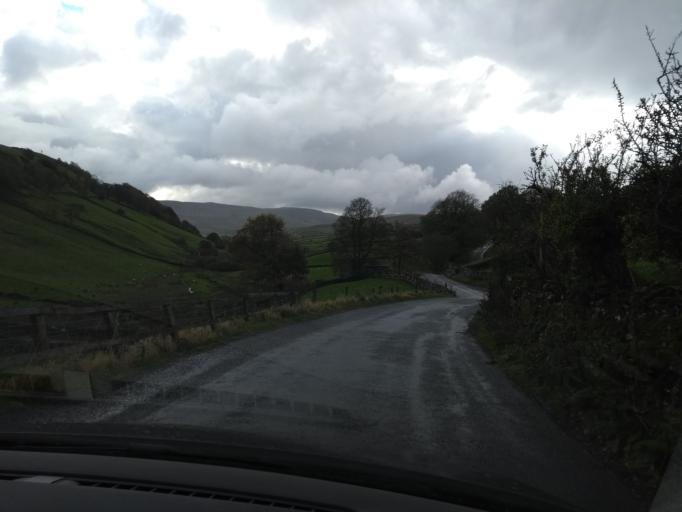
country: GB
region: England
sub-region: County Durham
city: Bowes
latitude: 54.4015
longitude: -2.1670
